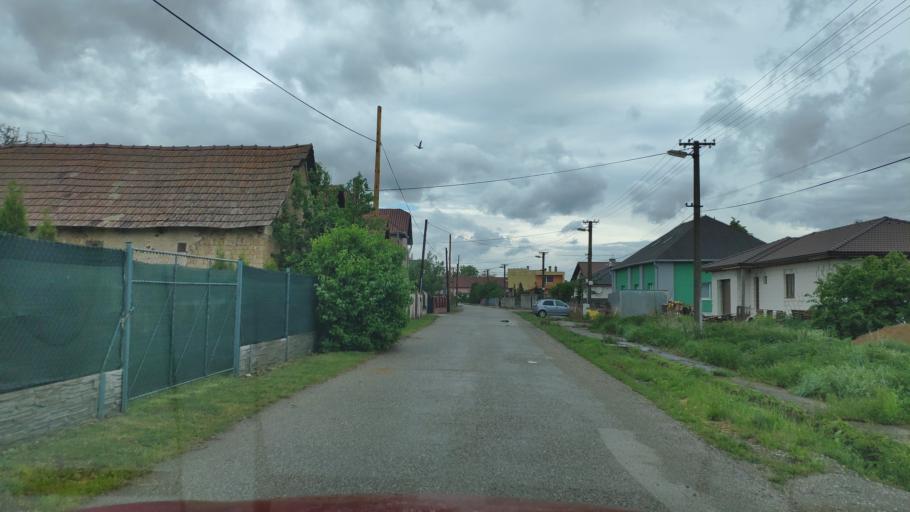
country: SK
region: Kosicky
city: Moldava nad Bodvou
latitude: 48.5712
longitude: 21.1218
